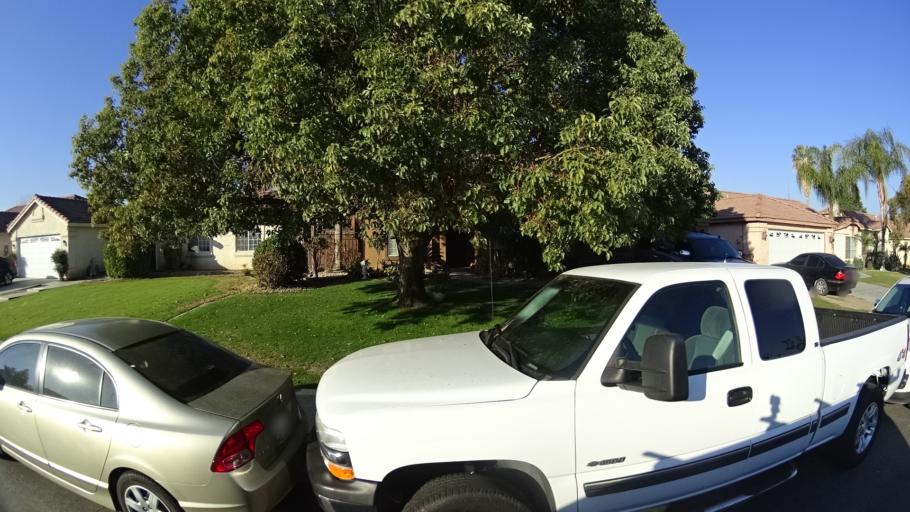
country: US
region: California
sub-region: Kern County
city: Greenfield
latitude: 35.2982
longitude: -119.0110
